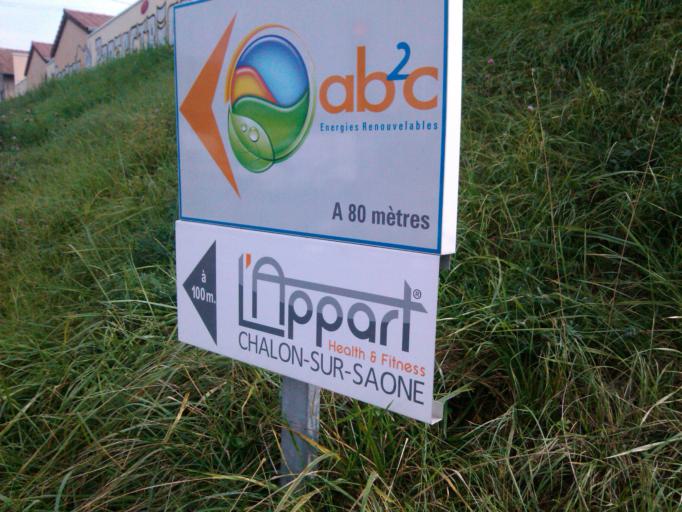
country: FR
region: Bourgogne
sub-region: Departement de Saone-et-Loire
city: Chatenoy-le-Royal
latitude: 46.7933
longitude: 4.8238
